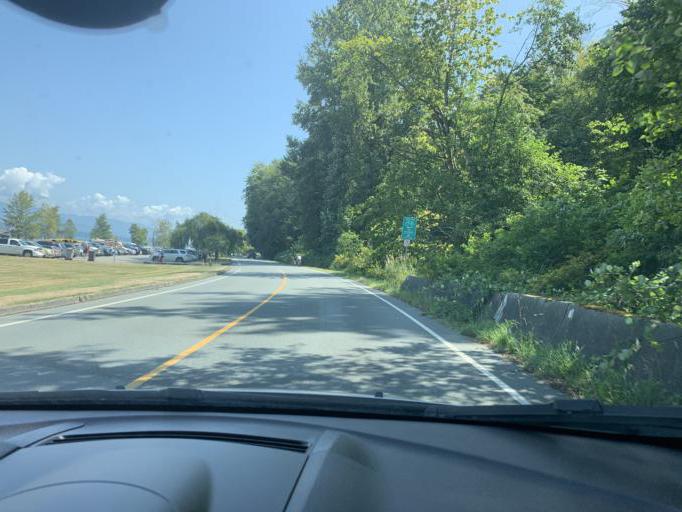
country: CA
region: British Columbia
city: West End
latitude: 49.2781
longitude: -123.2339
